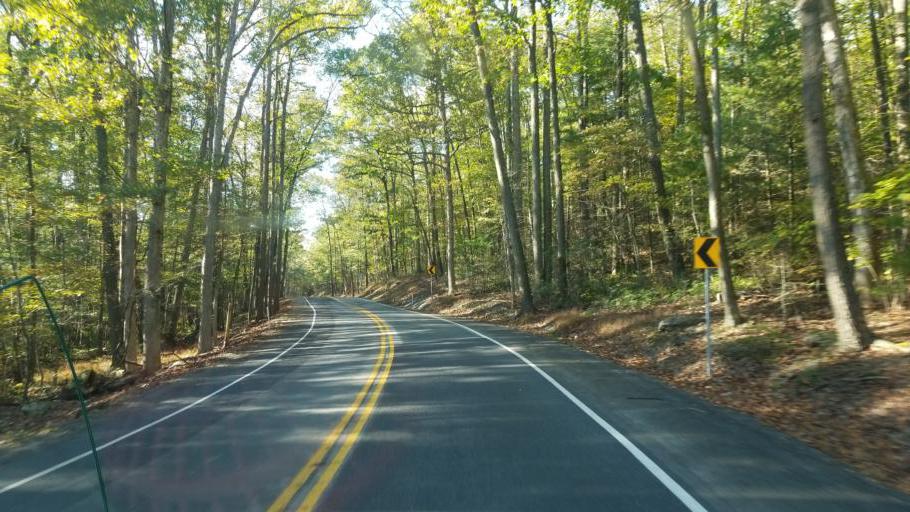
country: US
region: Pennsylvania
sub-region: Franklin County
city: Fayetteville
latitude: 39.8720
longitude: -77.4967
